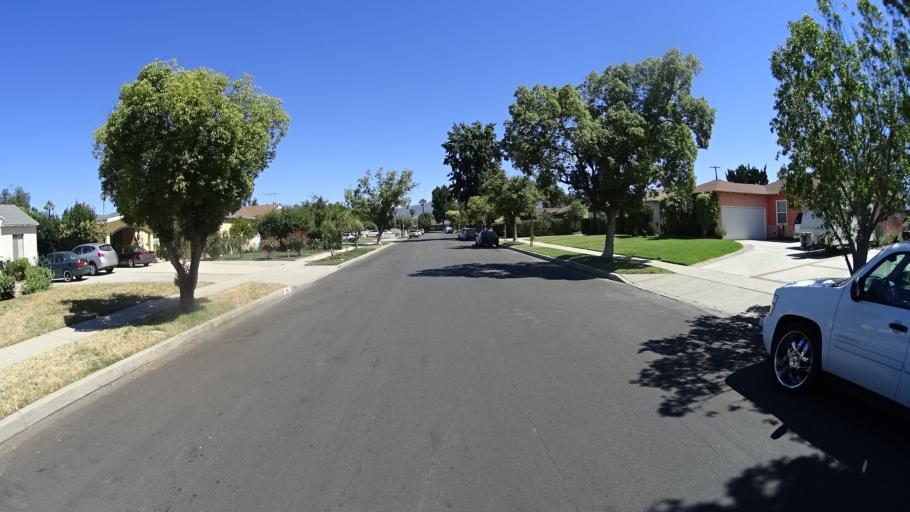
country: US
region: California
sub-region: Los Angeles County
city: San Fernando
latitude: 34.2547
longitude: -118.4630
